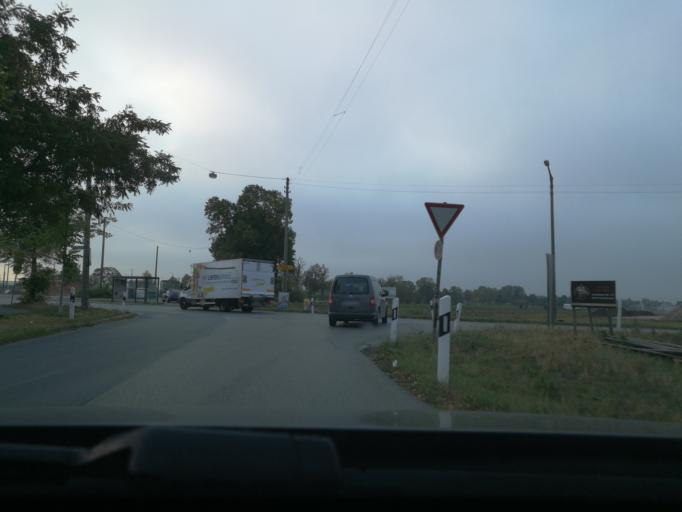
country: DE
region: Bavaria
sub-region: Regierungsbezirk Mittelfranken
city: Wetzendorf
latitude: 49.4928
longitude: 11.0501
